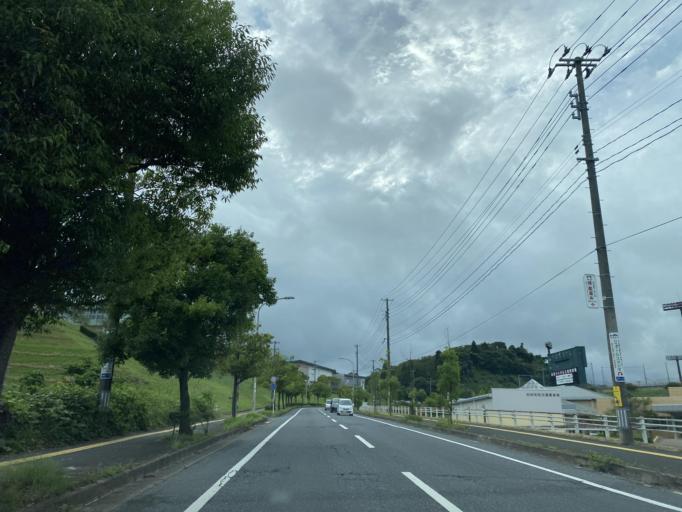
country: JP
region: Miyagi
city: Rifu
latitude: 38.3349
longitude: 140.9682
